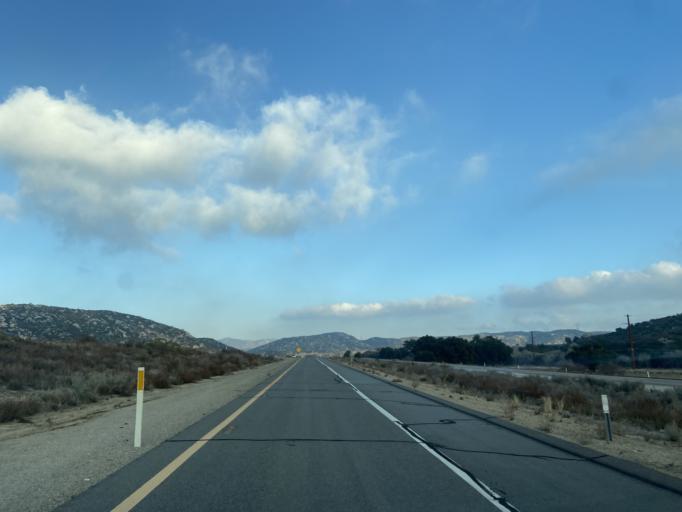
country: US
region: California
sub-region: San Diego County
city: Campo
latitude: 32.7175
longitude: -116.4680
